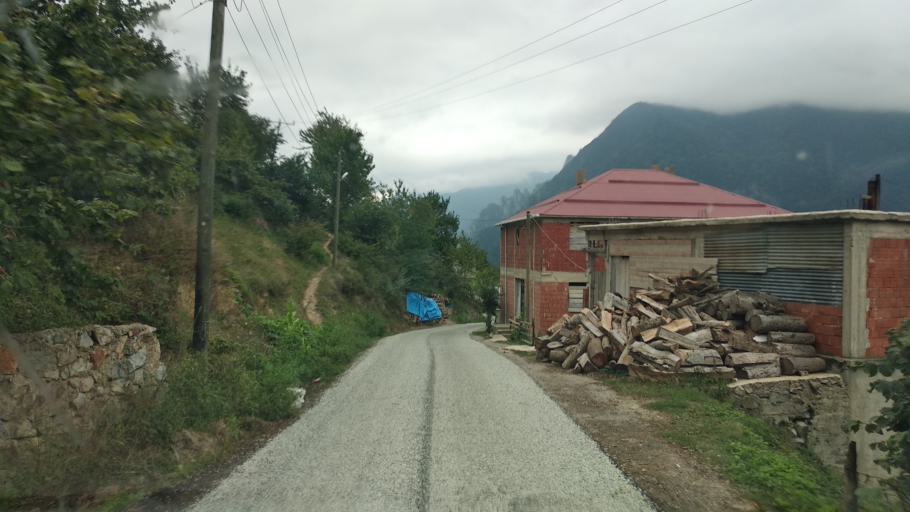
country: TR
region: Giresun
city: Dogankent
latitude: 40.7462
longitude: 38.9892
